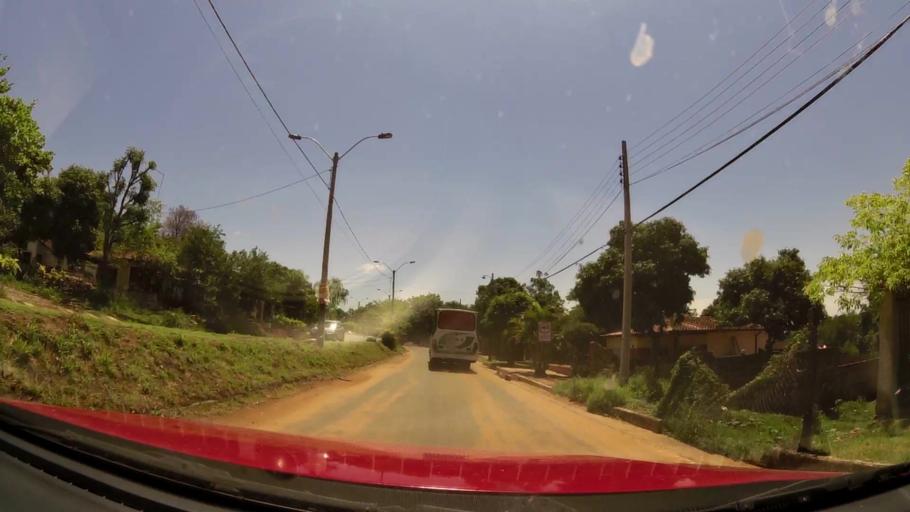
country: PY
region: Central
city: Colonia Mariano Roque Alonso
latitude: -25.2305
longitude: -57.5597
